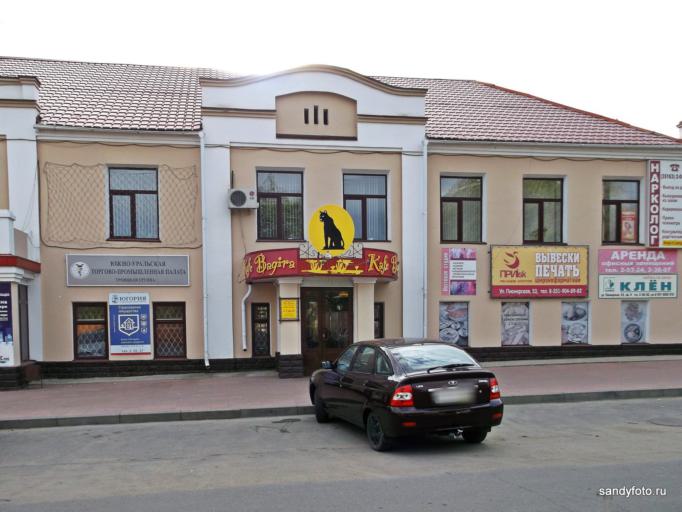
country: RU
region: Chelyabinsk
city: Troitsk
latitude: 54.0836
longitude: 61.5468
